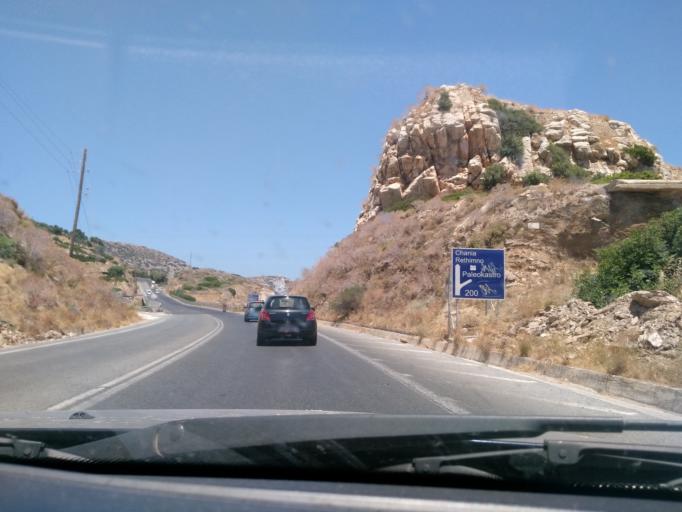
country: GR
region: Crete
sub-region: Nomos Irakleiou
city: Gazi
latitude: 35.3647
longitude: 25.0386
